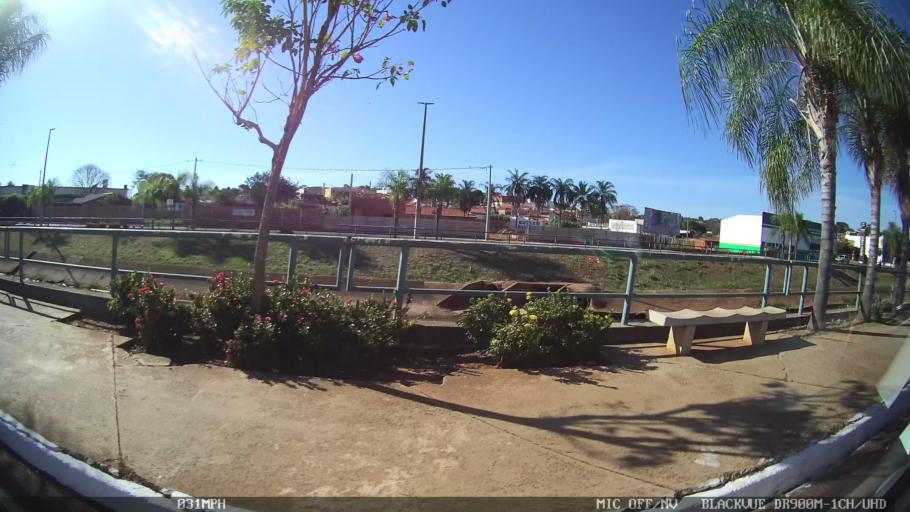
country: BR
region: Sao Paulo
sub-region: Olimpia
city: Olimpia
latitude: -20.7428
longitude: -48.9074
